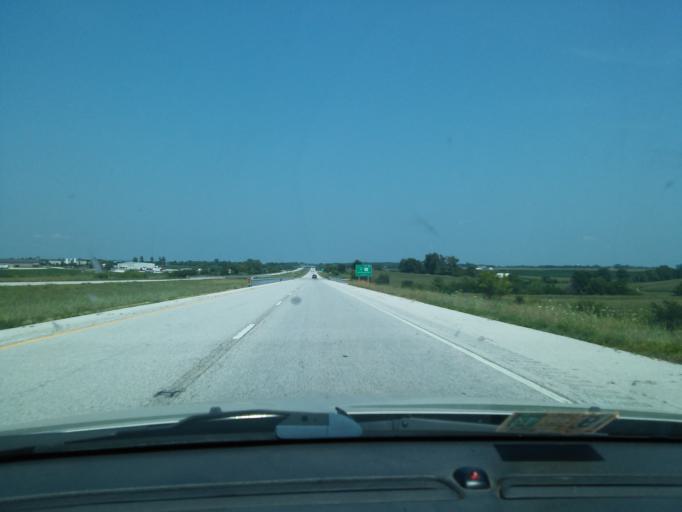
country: US
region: Illinois
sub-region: Morgan County
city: South Jacksonville
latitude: 39.7123
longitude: -90.1785
